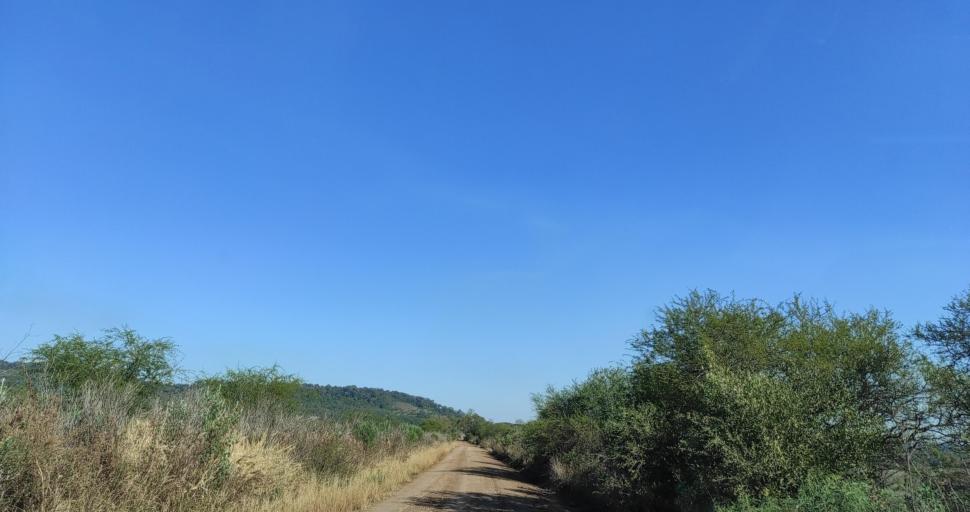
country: AR
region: Misiones
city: Cerro Cora
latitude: -27.6574
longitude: -55.6587
